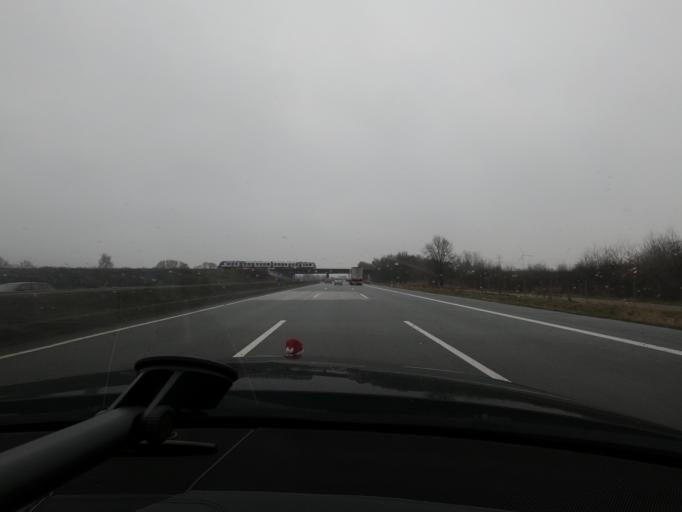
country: DE
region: Schleswig-Holstein
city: Grossenaspe
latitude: 53.9708
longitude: 9.9485
